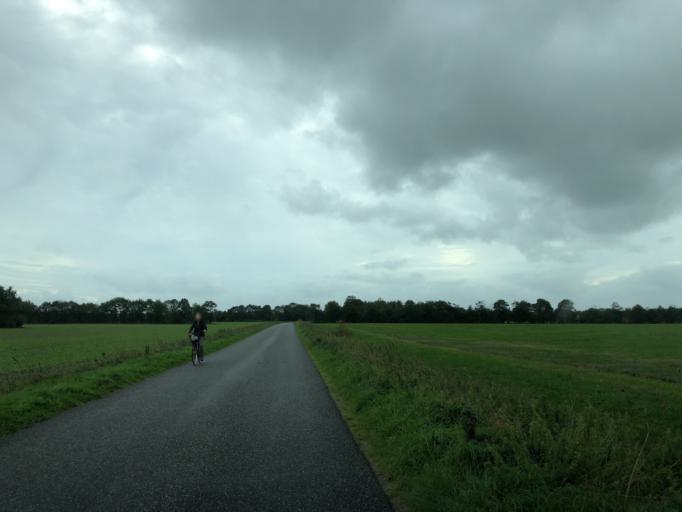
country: DK
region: Central Jutland
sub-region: Herning Kommune
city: Vildbjerg
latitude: 56.1968
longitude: 8.8205
